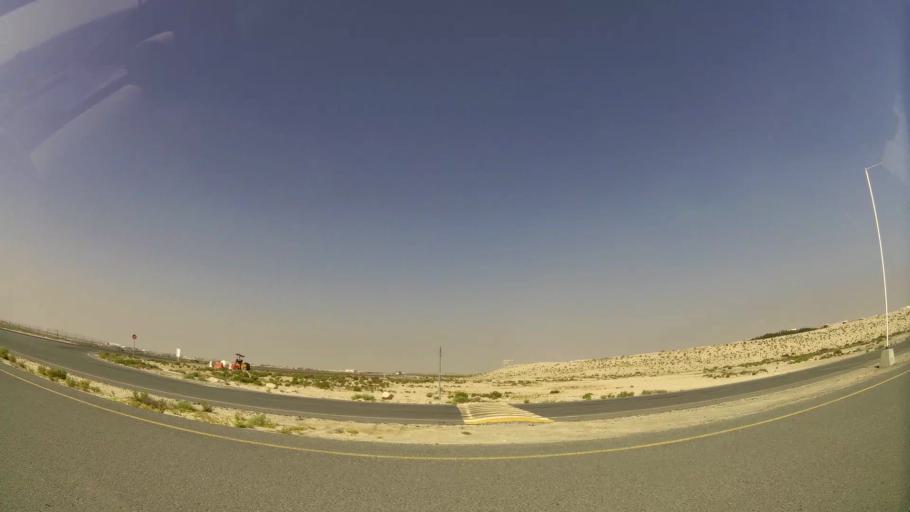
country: AE
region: Dubai
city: Dubai
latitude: 24.9588
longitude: 55.0167
